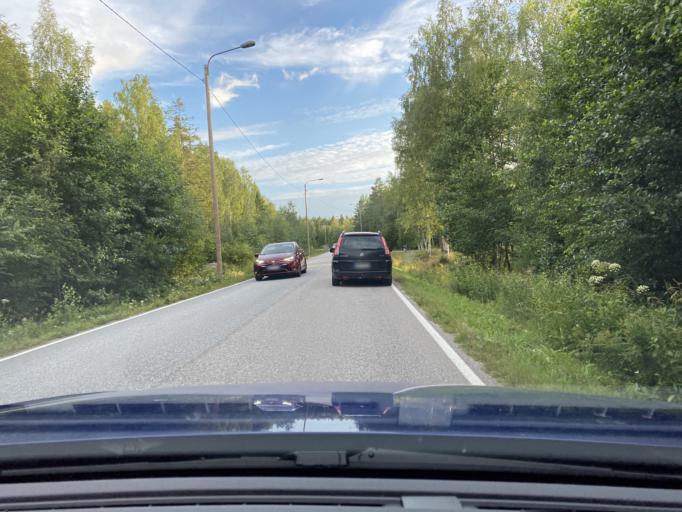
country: FI
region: Ostrobothnia
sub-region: Vaasa
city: Korsnaes
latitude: 62.9556
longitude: 21.1804
